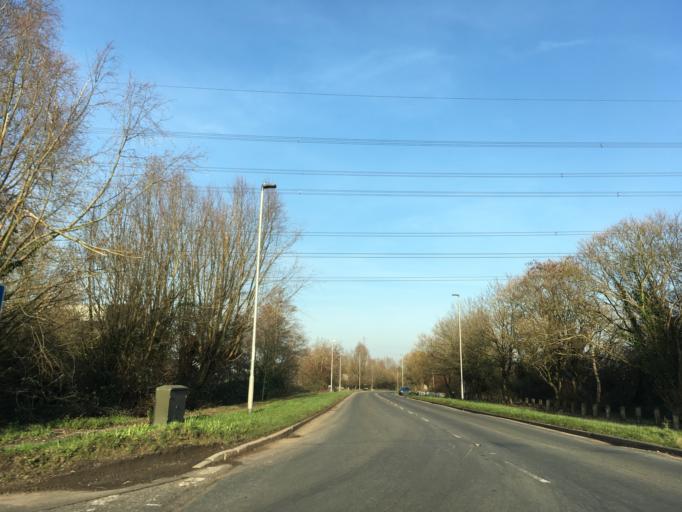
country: GB
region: Wales
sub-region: Newport
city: Nash
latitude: 51.5661
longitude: -2.9452
